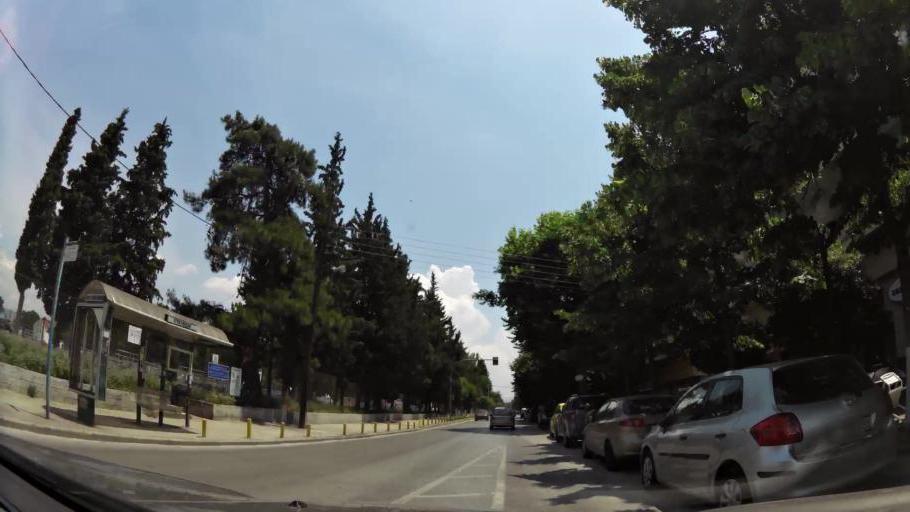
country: GR
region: Central Macedonia
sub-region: Nomos Thessalonikis
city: Ampelokipoi
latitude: 40.6571
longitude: 22.9146
